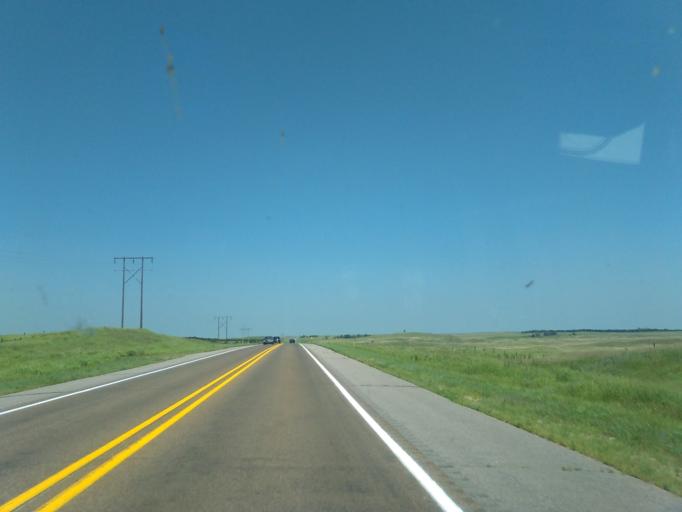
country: US
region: Nebraska
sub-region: Lincoln County
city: North Platte
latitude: 40.8775
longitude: -100.7540
